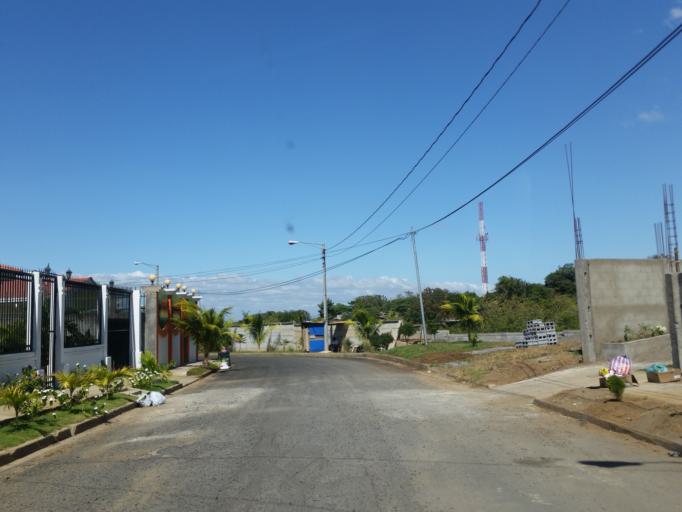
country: NI
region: Managua
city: Managua
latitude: 12.1071
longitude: -86.2423
